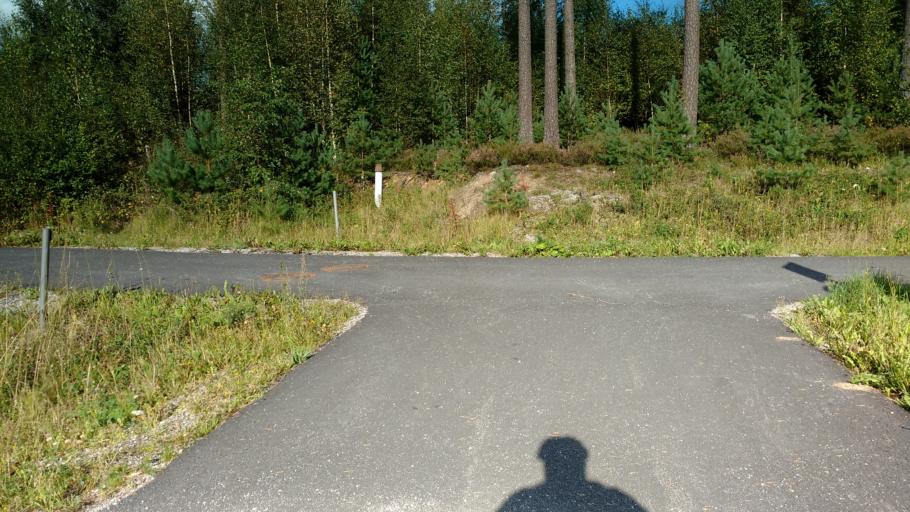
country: FI
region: Varsinais-Suomi
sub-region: Salo
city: Salo
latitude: 60.3804
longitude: 23.1915
